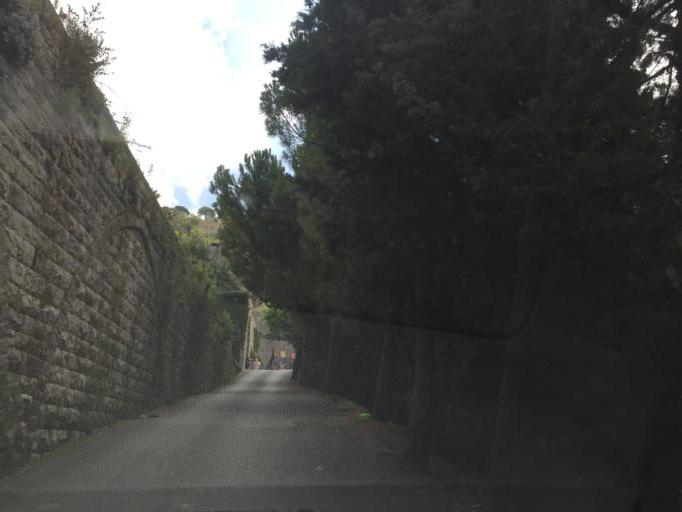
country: LB
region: Mont-Liban
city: Beit ed Dine
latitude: 33.6953
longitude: 35.5801
